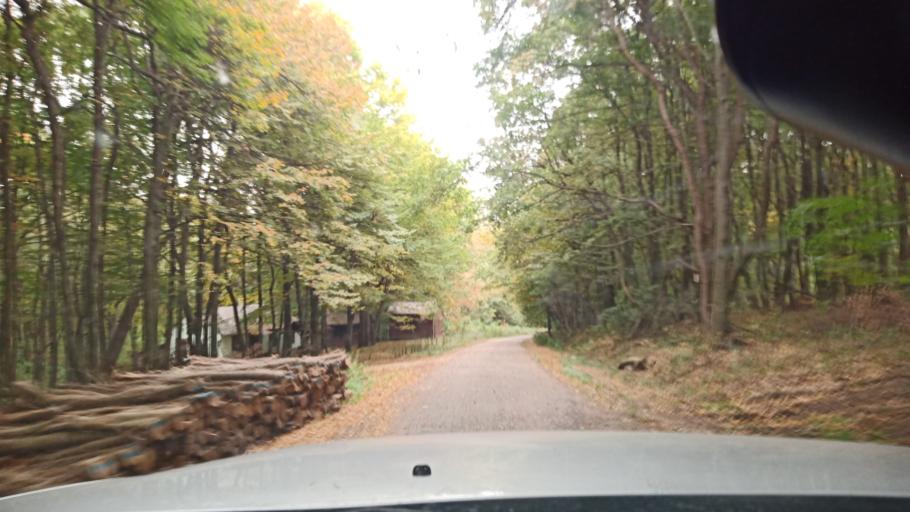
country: HU
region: Fejer
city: Pusztavam
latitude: 47.3845
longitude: 18.2795
